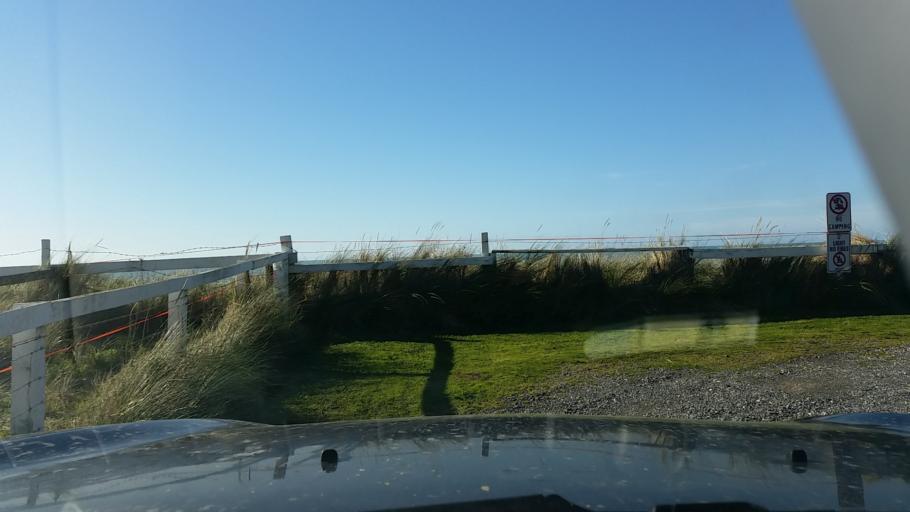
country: NZ
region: Marlborough
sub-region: Marlborough District
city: Blenheim
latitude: -41.6646
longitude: 174.1581
